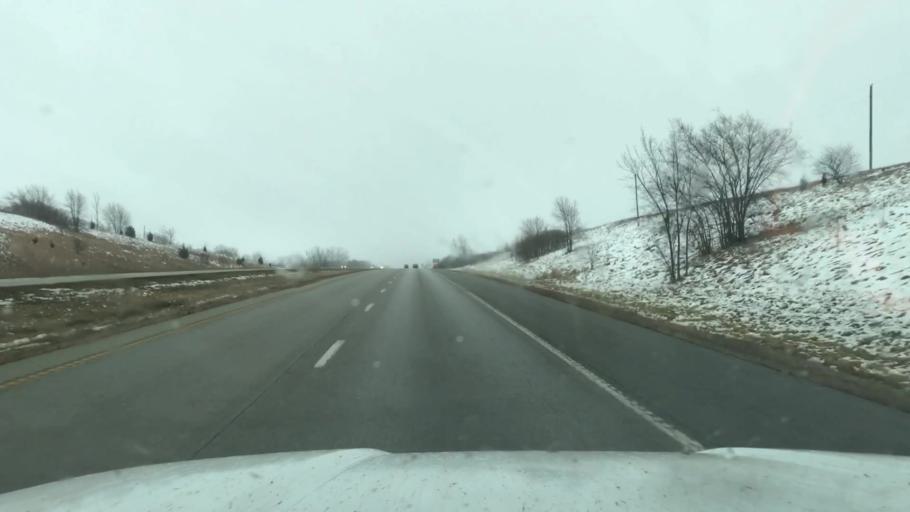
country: US
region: Missouri
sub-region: Buchanan County
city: Saint Joseph
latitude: 39.7476
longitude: -94.7070
